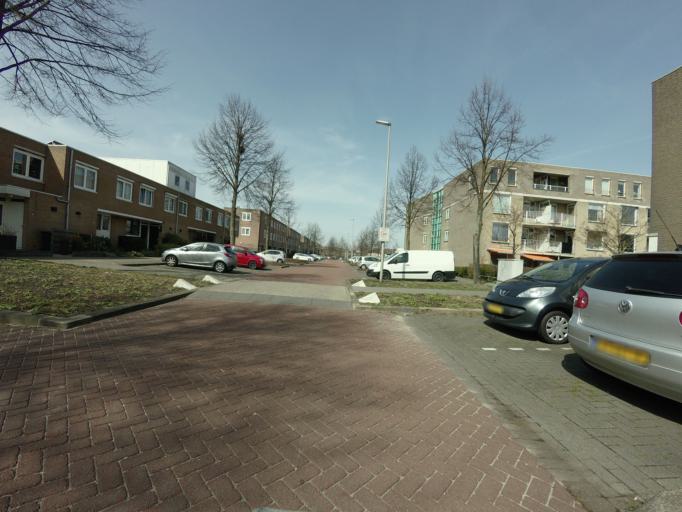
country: NL
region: South Holland
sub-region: Gemeente Zoetermeer
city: Zoetermeer
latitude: 52.0745
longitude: 4.5158
